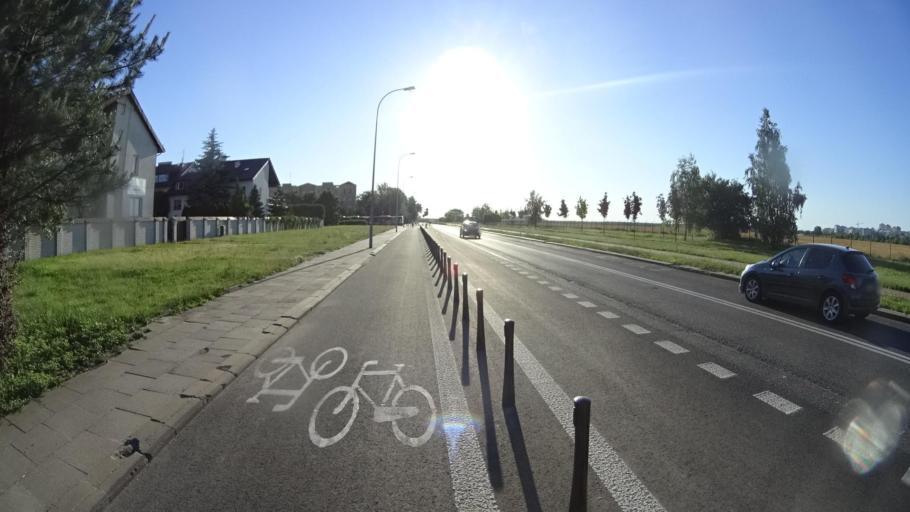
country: PL
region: Masovian Voivodeship
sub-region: Warszawa
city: Bemowo
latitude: 52.2643
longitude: 20.9216
